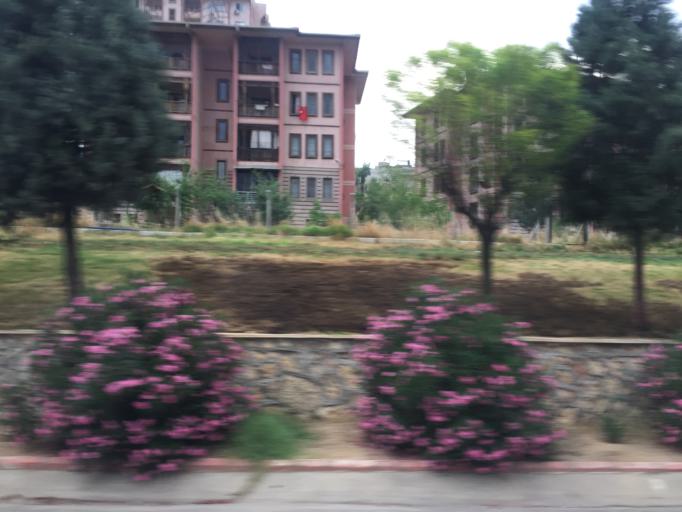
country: TR
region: Gaziantep
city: Gaziantep
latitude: 37.0452
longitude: 37.4247
